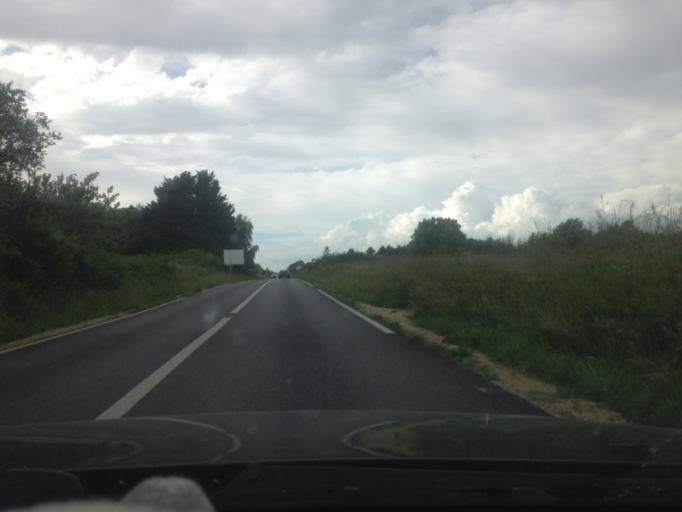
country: FR
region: Brittany
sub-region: Departement du Morbihan
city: Plouharnel
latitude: 47.6142
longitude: -3.1289
